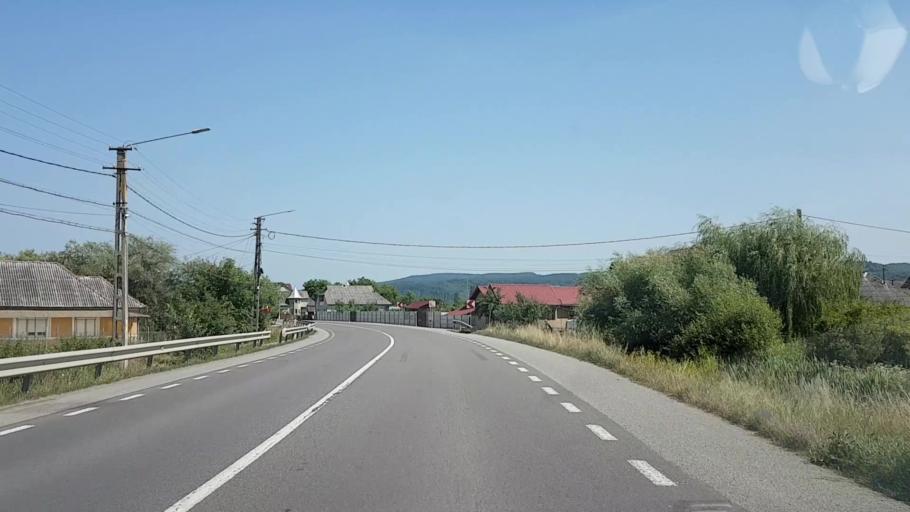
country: RO
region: Bistrita-Nasaud
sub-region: Comuna Uriu
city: Cristestii Ciceului
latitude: 47.1918
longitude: 24.0973
